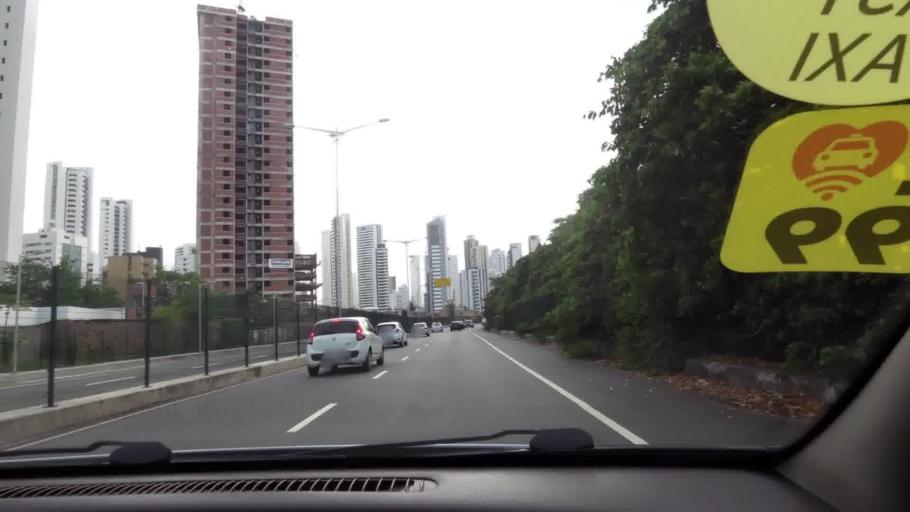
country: BR
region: Pernambuco
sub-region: Recife
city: Recife
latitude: -8.1067
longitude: -34.8935
